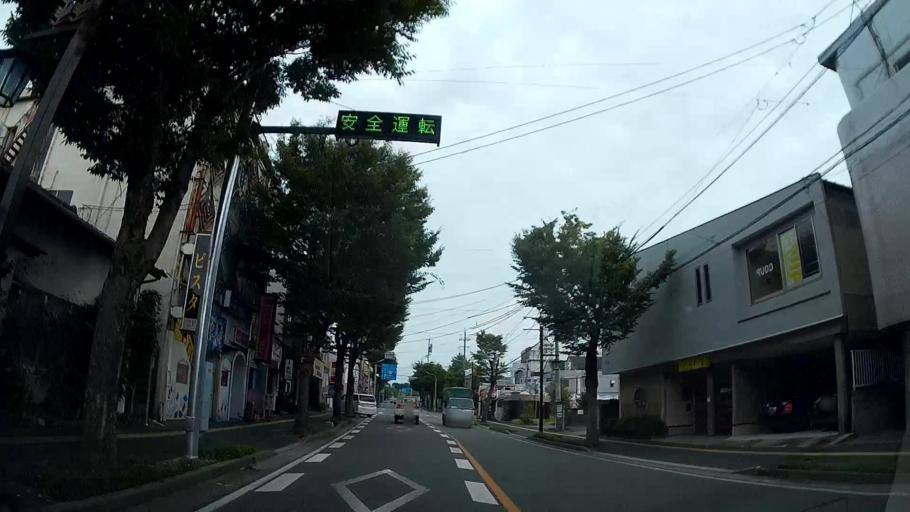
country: JP
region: Kumamoto
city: Kikuchi
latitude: 32.9832
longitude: 130.8151
